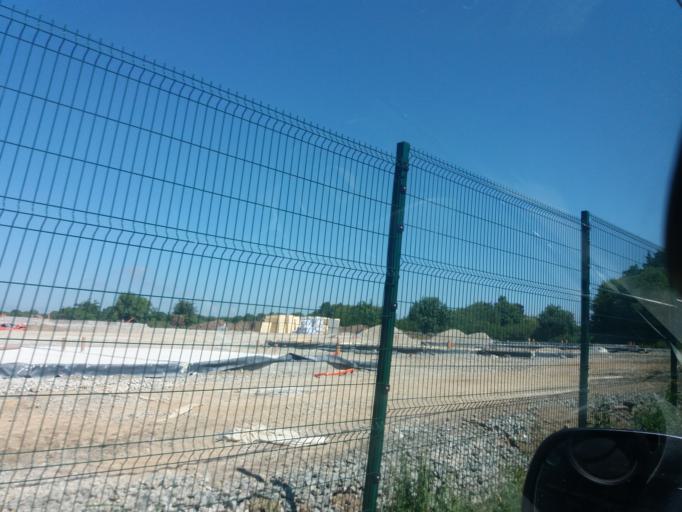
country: IE
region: Leinster
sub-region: Fingal County
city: Swords
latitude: 53.5228
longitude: -6.2649
